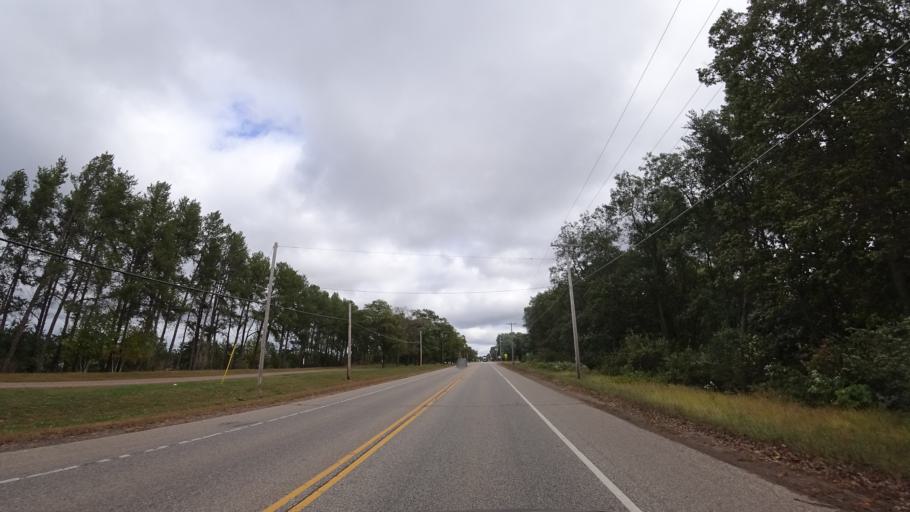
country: US
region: Wisconsin
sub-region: Chippewa County
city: Lake Wissota
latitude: 44.9264
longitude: -91.3104
